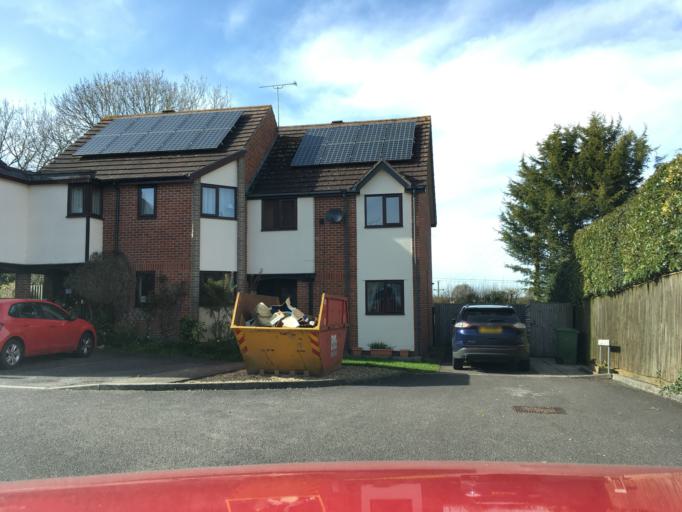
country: GB
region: England
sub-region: Wiltshire
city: Chippenham
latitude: 51.4874
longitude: -2.1263
